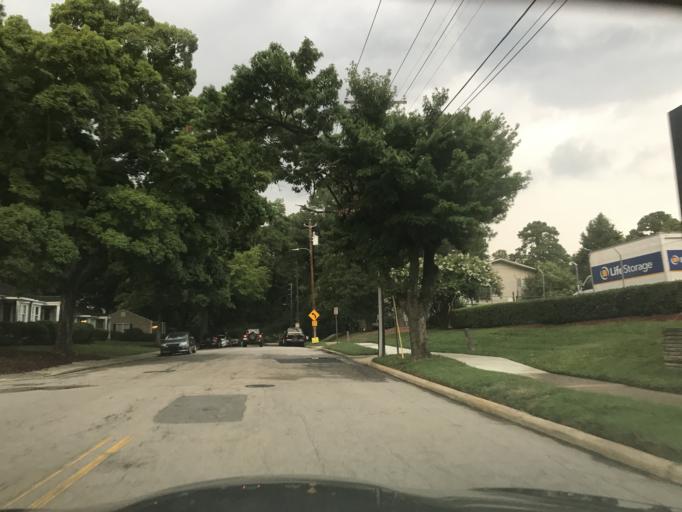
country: US
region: North Carolina
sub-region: Wake County
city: Raleigh
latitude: 35.8142
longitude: -78.6290
